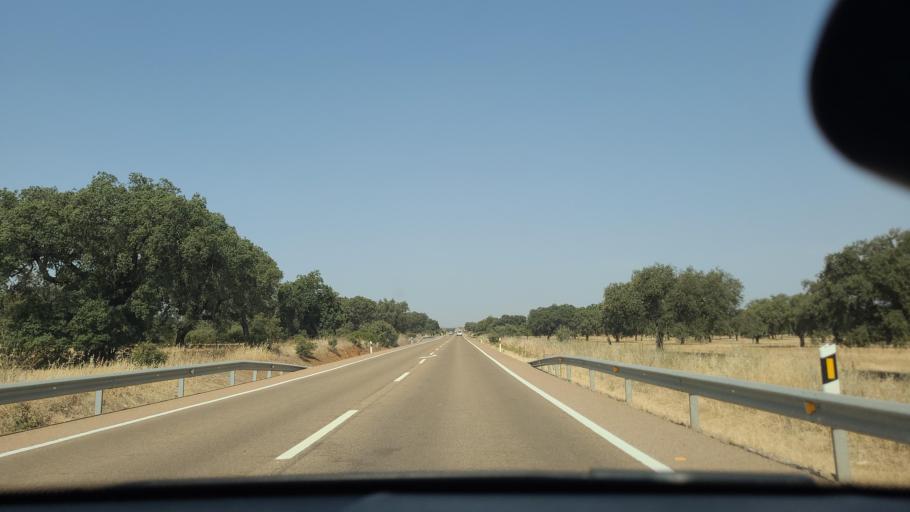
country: ES
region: Extremadura
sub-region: Provincia de Badajoz
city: Usagre
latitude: 38.3669
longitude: -6.2370
